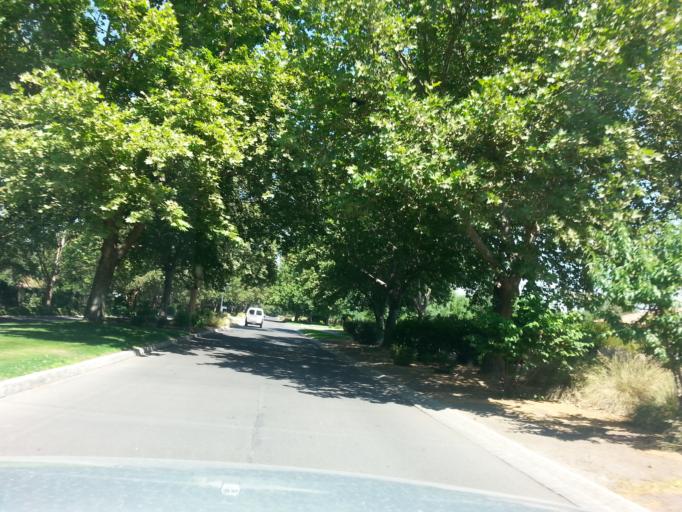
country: CL
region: Santiago Metropolitan
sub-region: Provincia de Chacabuco
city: Chicureo Abajo
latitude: -33.2429
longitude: -70.6811
